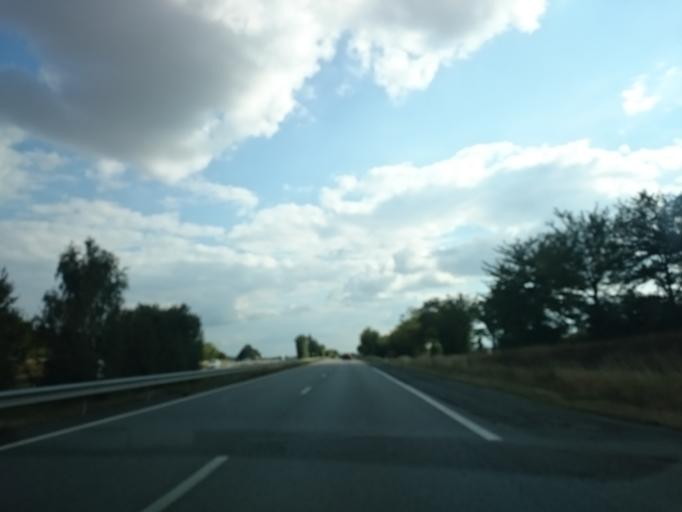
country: FR
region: Brittany
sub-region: Departement d'Ille-et-Vilaine
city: Crevin
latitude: 47.9143
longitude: -1.6819
